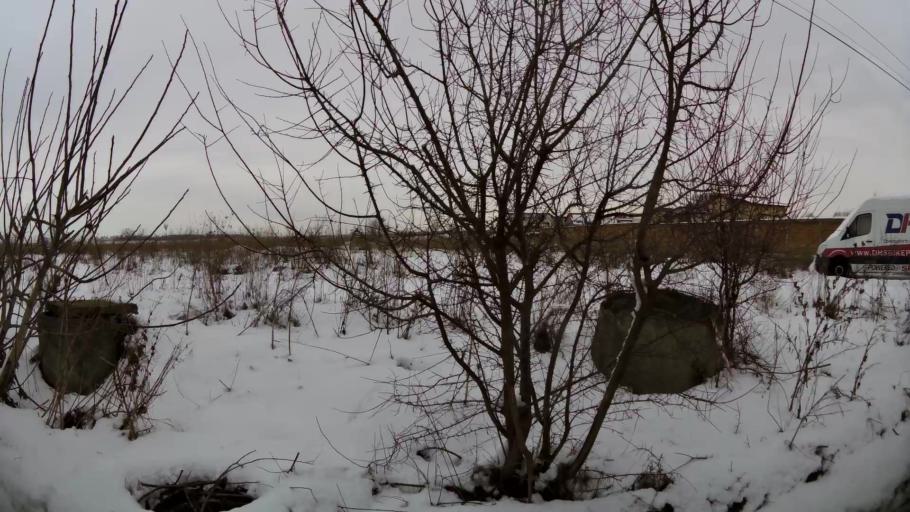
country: RO
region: Ilfov
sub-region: Comuna Tunari
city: Tunari
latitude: 44.5179
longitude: 26.1460
